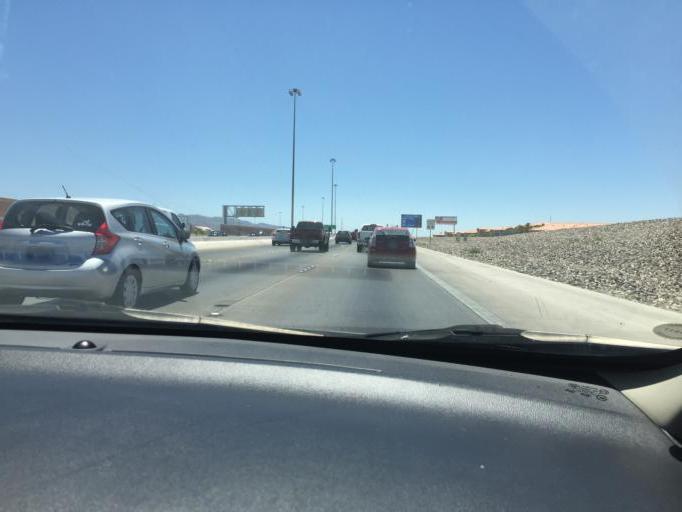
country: US
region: Nevada
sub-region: Clark County
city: Whitney
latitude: 36.0332
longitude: -115.1327
